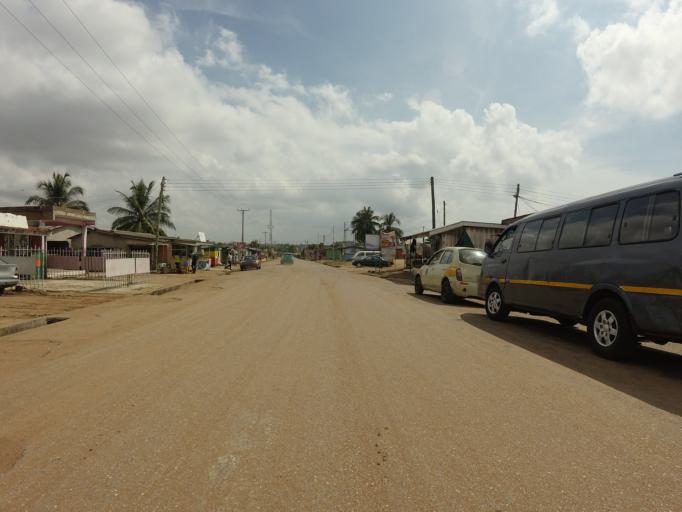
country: GH
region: Greater Accra
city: Nungua
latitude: 5.6093
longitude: -0.0833
